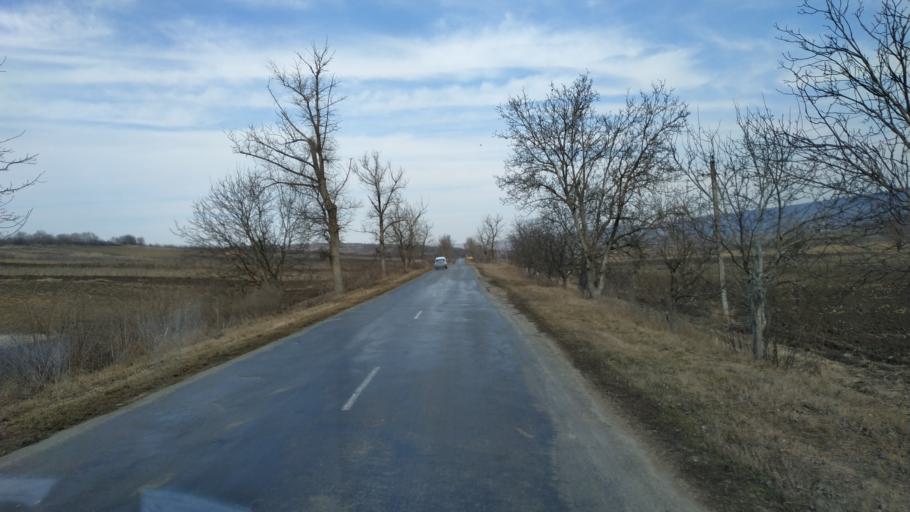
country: MD
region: Nisporeni
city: Nisporeni
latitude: 47.1151
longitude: 28.1229
